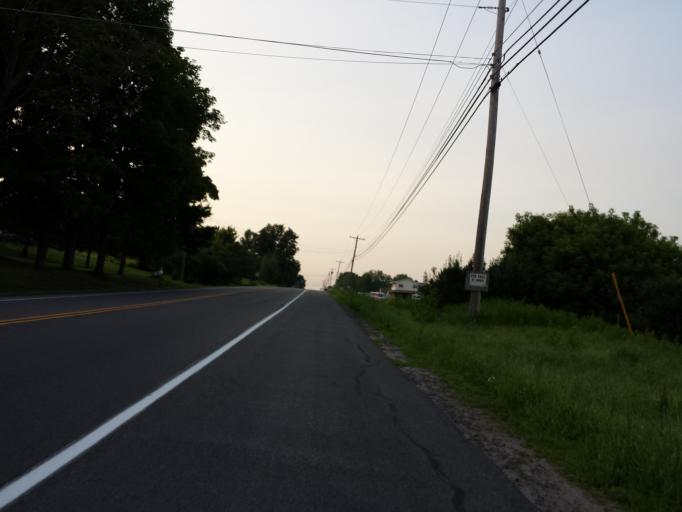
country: US
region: New York
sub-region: St. Lawrence County
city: Potsdam
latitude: 44.7067
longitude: -74.9871
